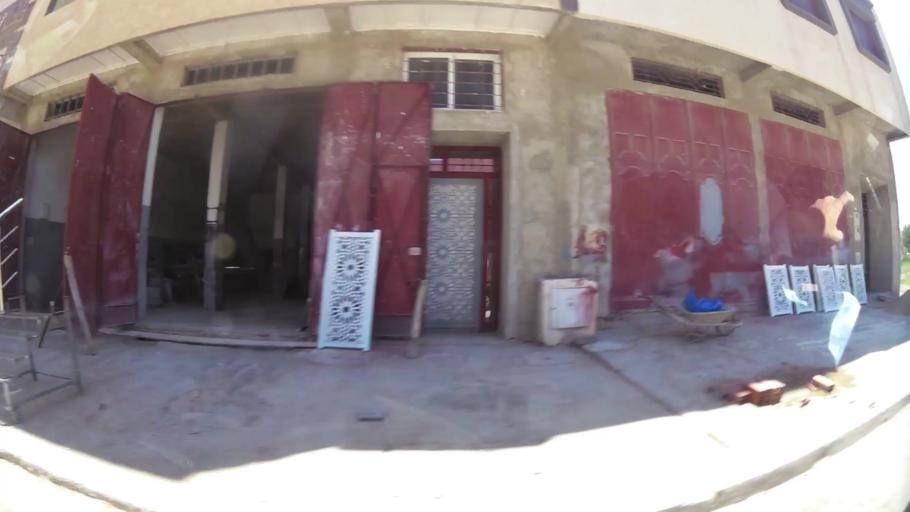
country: MA
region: Oriental
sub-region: Oujda-Angad
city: Oujda
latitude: 34.6590
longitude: -1.9529
